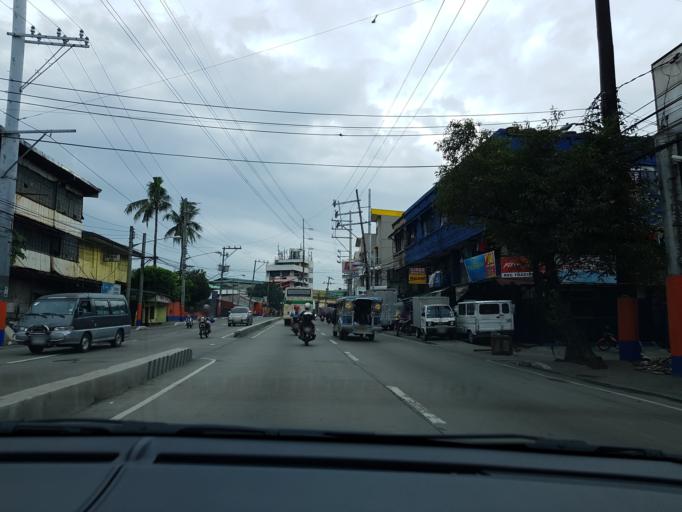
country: PH
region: Metro Manila
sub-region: Caloocan City
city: Niugan
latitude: 14.6666
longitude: 120.9834
